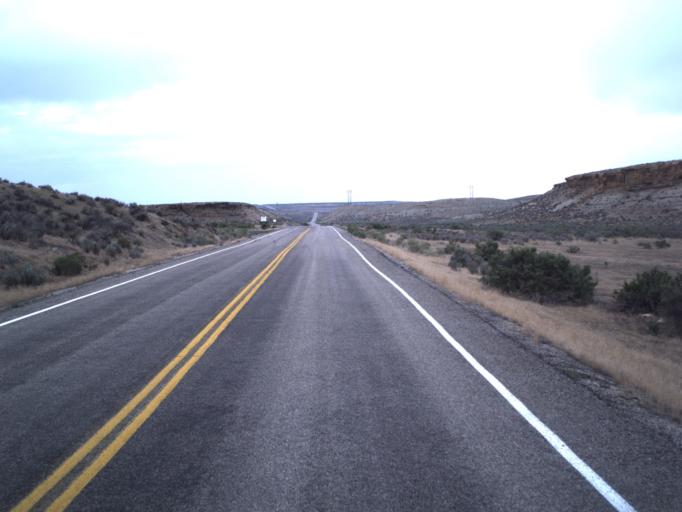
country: US
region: Colorado
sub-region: Rio Blanco County
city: Rangely
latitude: 40.0465
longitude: -109.1877
